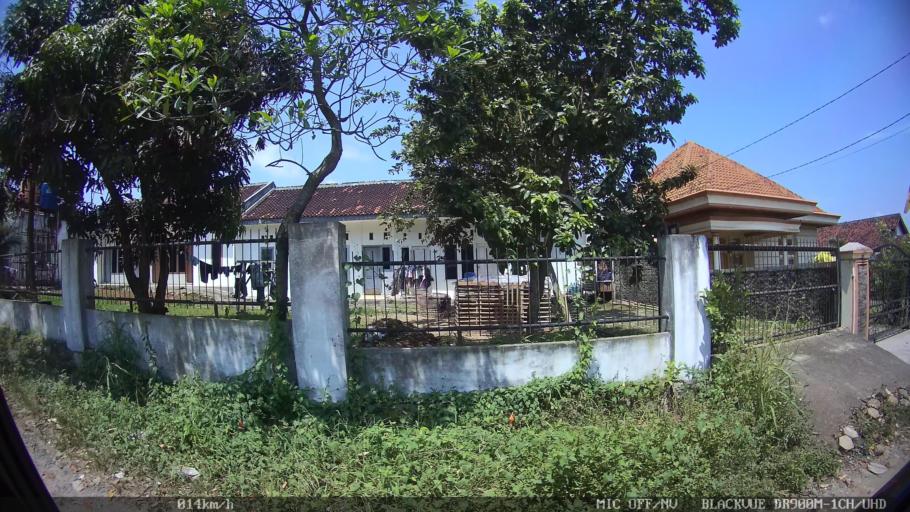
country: ID
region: Lampung
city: Kedaton
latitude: -5.3572
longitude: 105.2771
